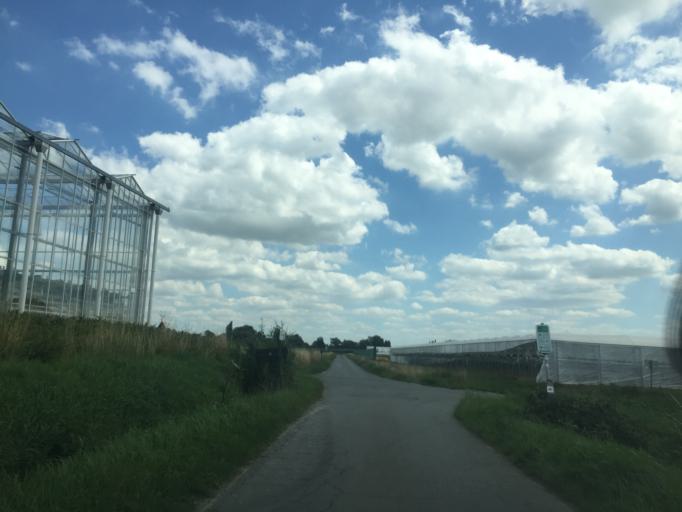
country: BE
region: Flanders
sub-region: Provincie West-Vlaanderen
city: Staden
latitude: 50.9950
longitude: 3.0116
